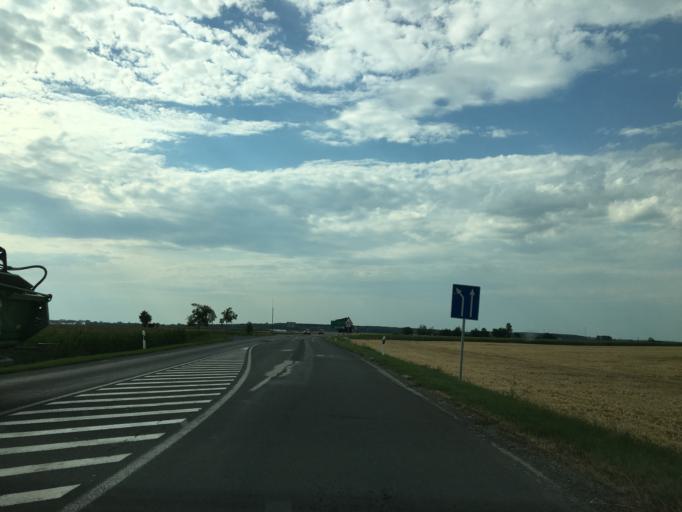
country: HU
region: Bacs-Kiskun
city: Dusnok
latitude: 46.4189
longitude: 18.9439
